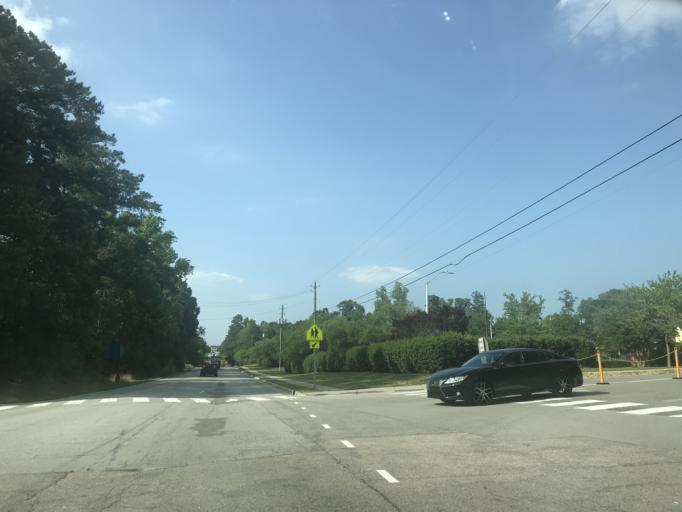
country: US
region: North Carolina
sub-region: Wake County
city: Knightdale
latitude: 35.8023
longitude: -78.4865
